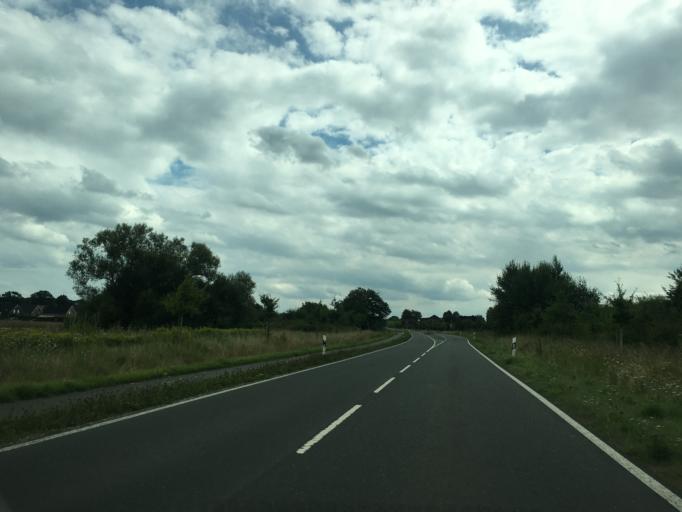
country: DE
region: North Rhine-Westphalia
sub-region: Regierungsbezirk Munster
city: Nordkirchen
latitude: 51.7368
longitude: 7.5102
